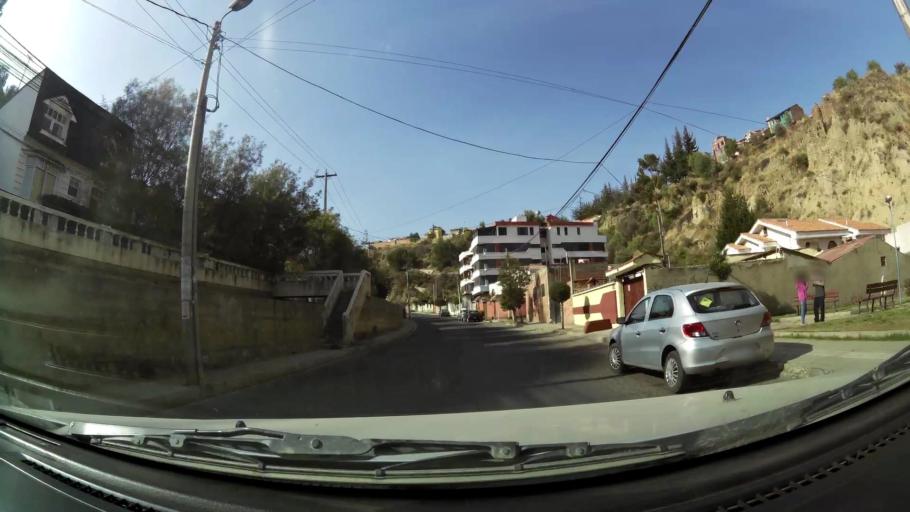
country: BO
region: La Paz
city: La Paz
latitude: -16.5300
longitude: -68.0788
